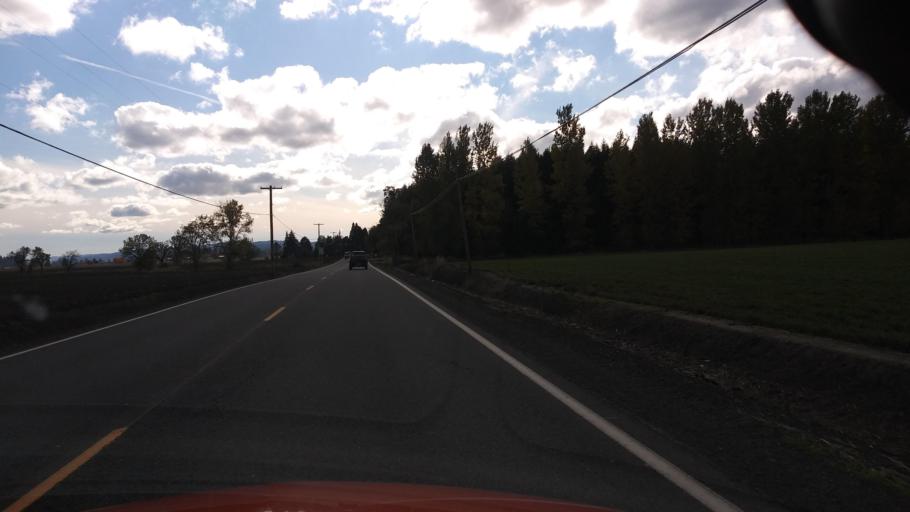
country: US
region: Oregon
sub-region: Washington County
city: Forest Grove
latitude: 45.5615
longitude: -123.1057
